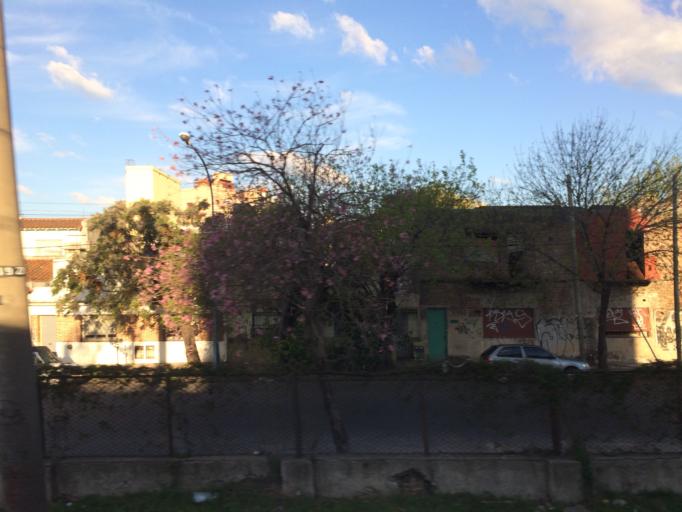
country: AR
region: Buenos Aires
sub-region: Partido de Lanus
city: Lanus
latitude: -34.7122
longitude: -58.3919
